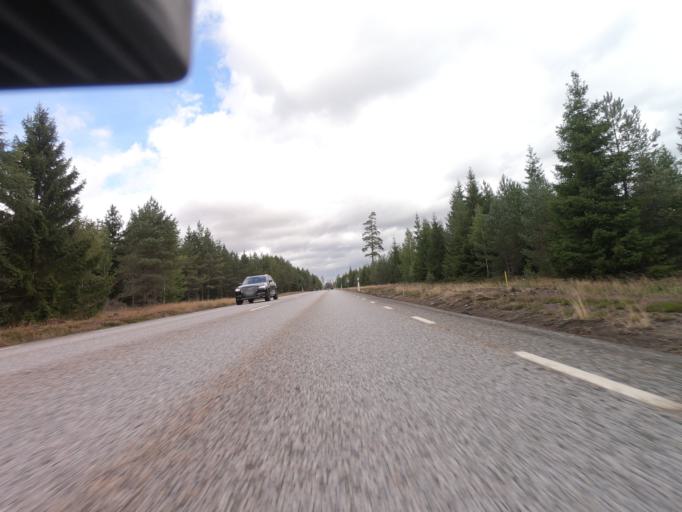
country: SE
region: Joenkoeping
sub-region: Vaggeryds Kommun
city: Vaggeryd
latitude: 57.5981
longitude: 14.2205
